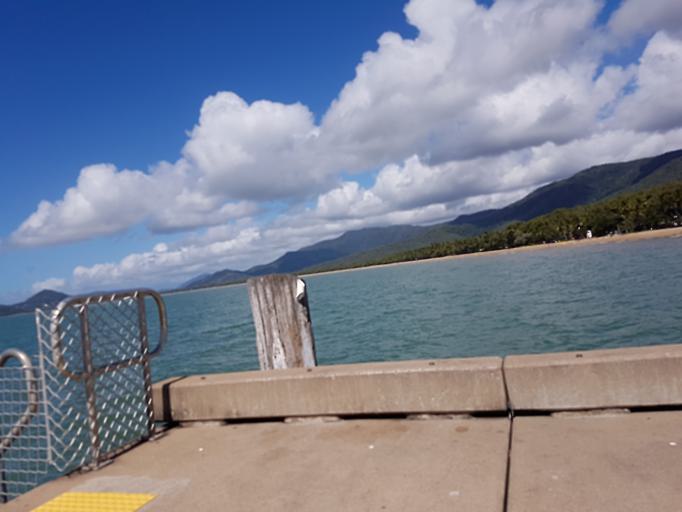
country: AU
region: Queensland
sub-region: Cairns
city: Palm Cove
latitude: -16.7399
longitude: 145.6730
